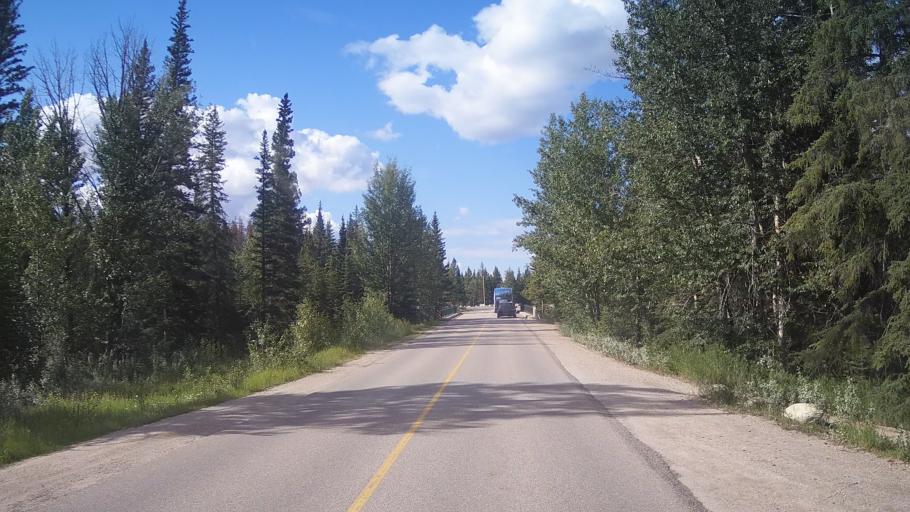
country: CA
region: Alberta
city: Jasper Park Lodge
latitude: 52.8646
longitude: -118.0704
